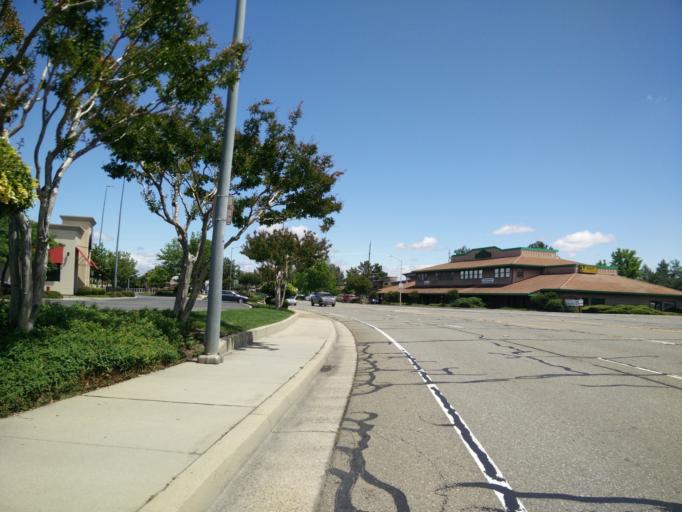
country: US
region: California
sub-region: Shasta County
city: Redding
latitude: 40.5860
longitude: -122.3554
